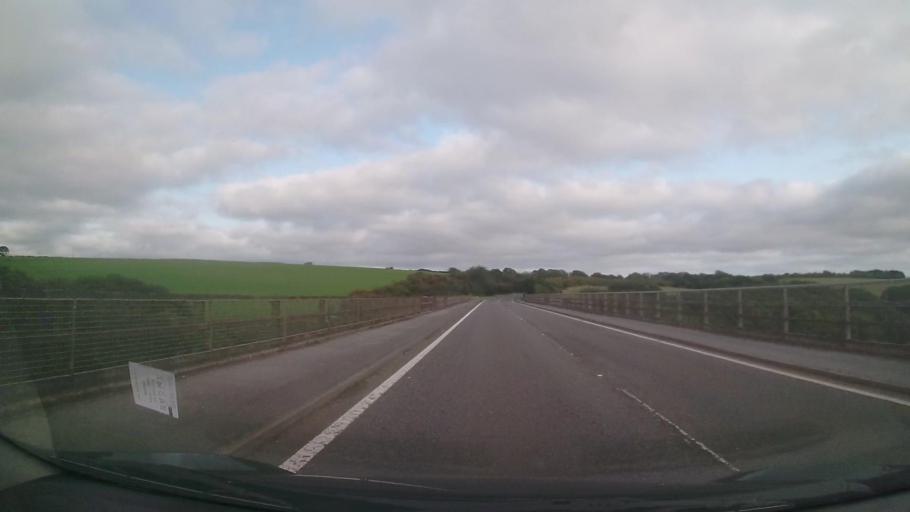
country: GB
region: Wales
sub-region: Pembrokeshire
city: Neyland
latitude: 51.7162
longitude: -4.9430
